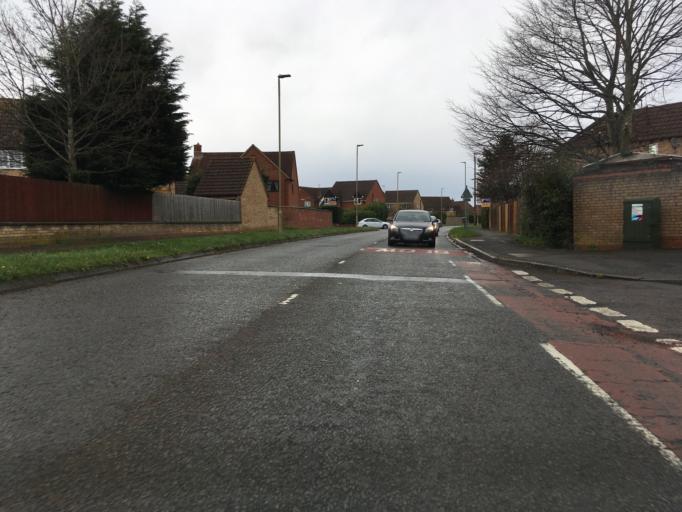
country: GB
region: England
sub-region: Gloucestershire
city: Gloucester
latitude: 51.8250
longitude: -2.2909
